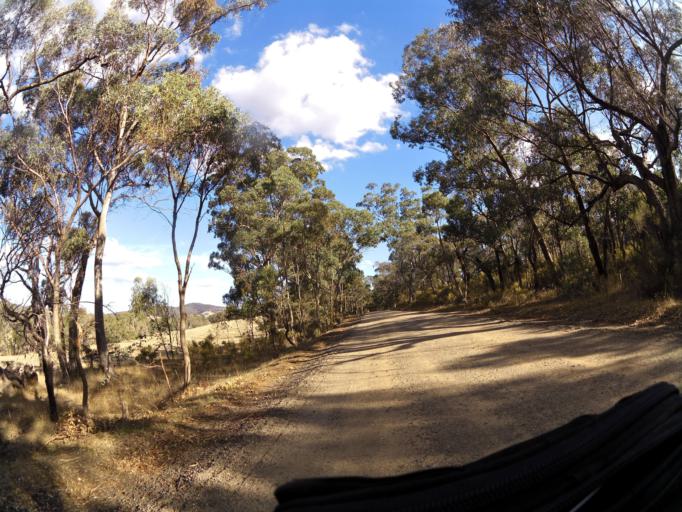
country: AU
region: Victoria
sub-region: Greater Bendigo
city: Kennington
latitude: -37.0146
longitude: 144.8080
